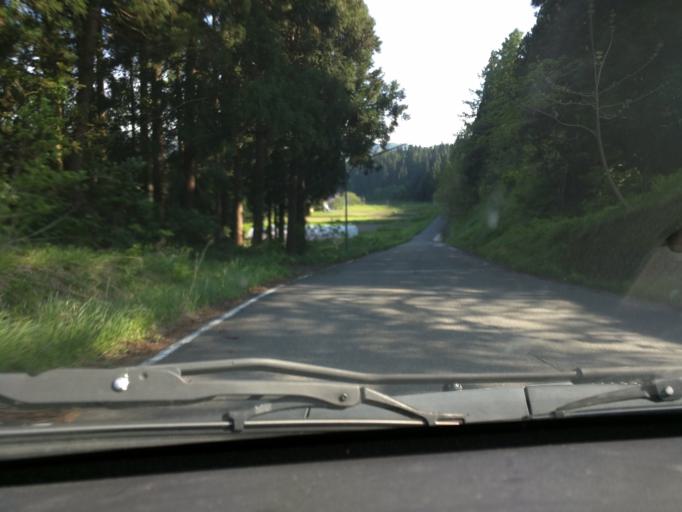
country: JP
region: Fukushima
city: Kitakata
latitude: 37.4915
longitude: 139.6643
